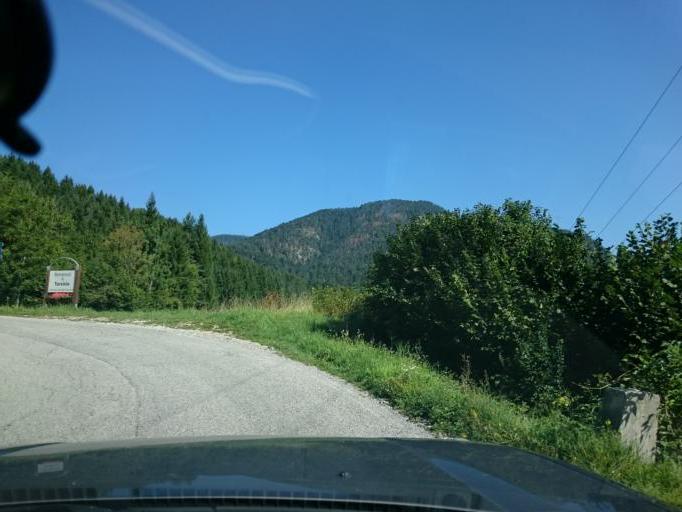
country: IT
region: Friuli Venezia Giulia
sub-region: Provincia di Udine
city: Tarvisio
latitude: 46.4986
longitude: 13.5889
